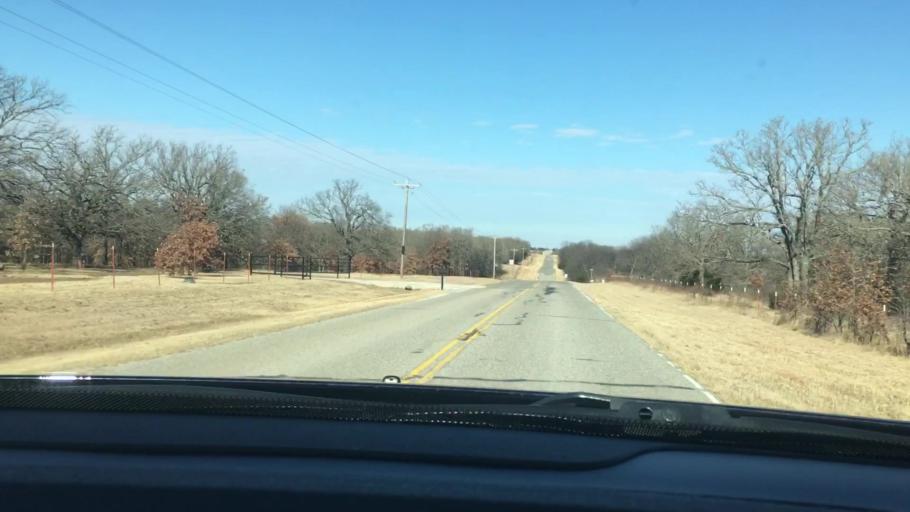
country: US
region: Oklahoma
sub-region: Garvin County
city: Wynnewood
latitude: 34.6643
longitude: -97.1254
